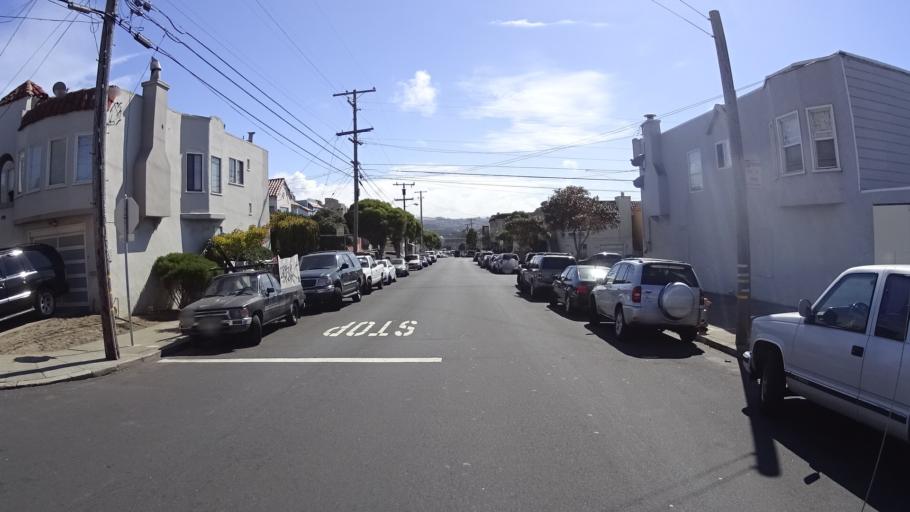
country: US
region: California
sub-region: San Mateo County
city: Daly City
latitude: 37.6944
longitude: -122.4659
